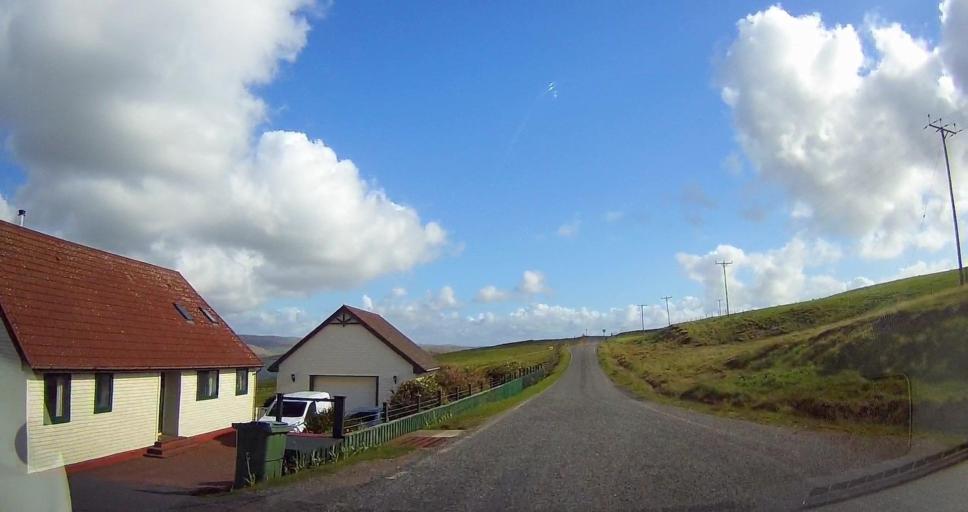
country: GB
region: Scotland
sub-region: Shetland Islands
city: Lerwick
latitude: 60.3832
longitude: -1.3789
